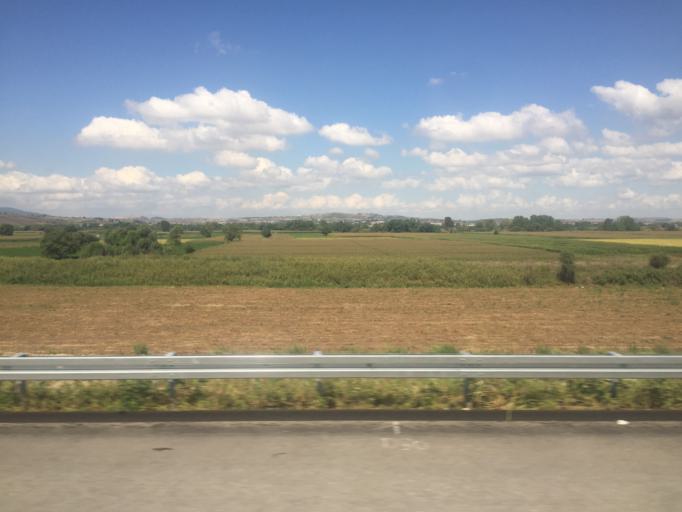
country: TR
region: Balikesir
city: Gobel
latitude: 40.0103
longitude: 28.1974
